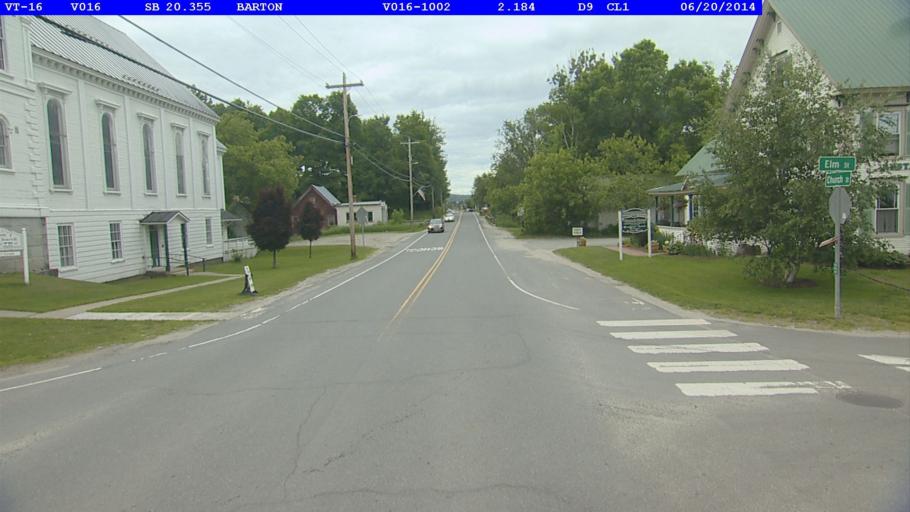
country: US
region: Vermont
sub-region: Orleans County
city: Newport
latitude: 44.7484
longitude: -72.1806
